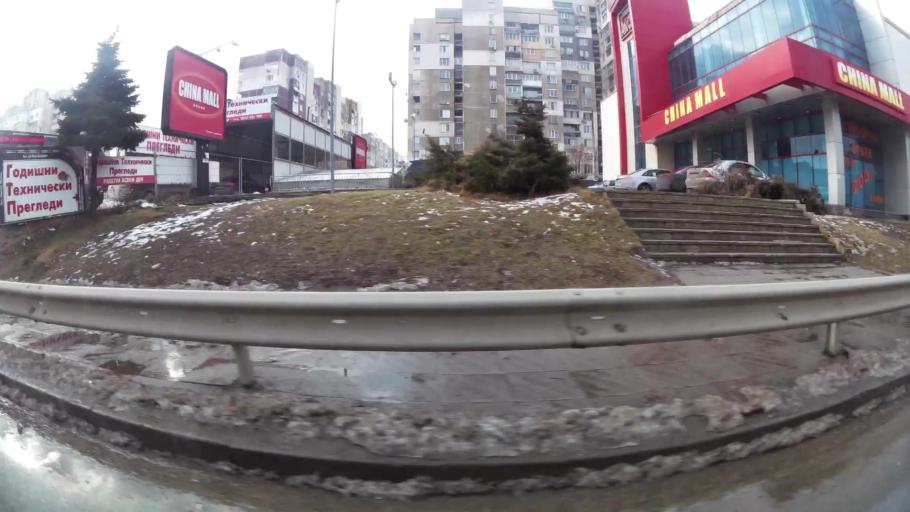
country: BG
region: Sofia-Capital
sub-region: Stolichna Obshtina
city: Sofia
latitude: 42.7128
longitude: 23.2673
